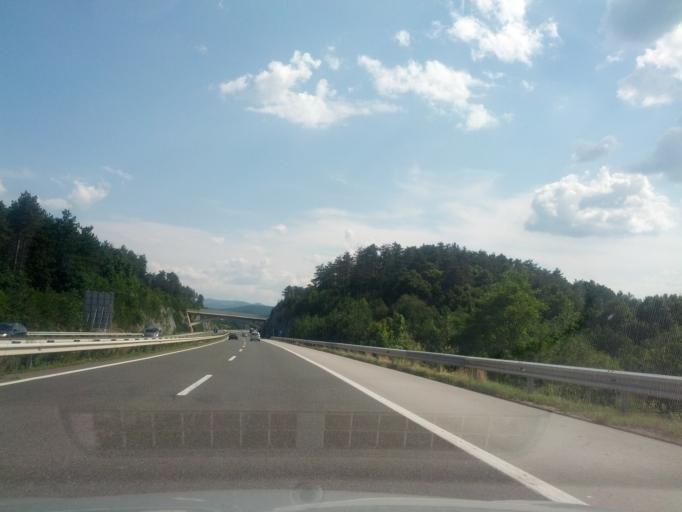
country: SI
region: Divaca
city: Divaca
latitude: 45.6900
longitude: 13.9775
